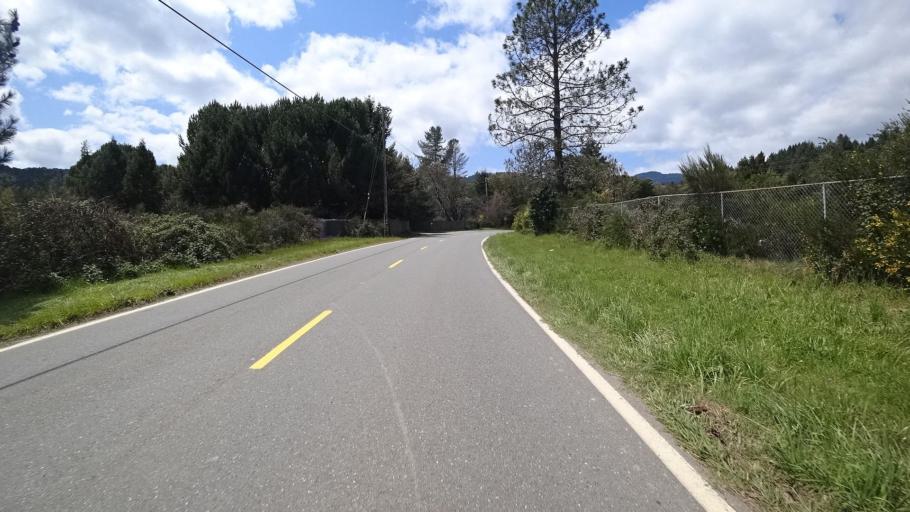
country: US
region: California
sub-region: Humboldt County
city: Redway
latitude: 40.0583
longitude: -123.9711
